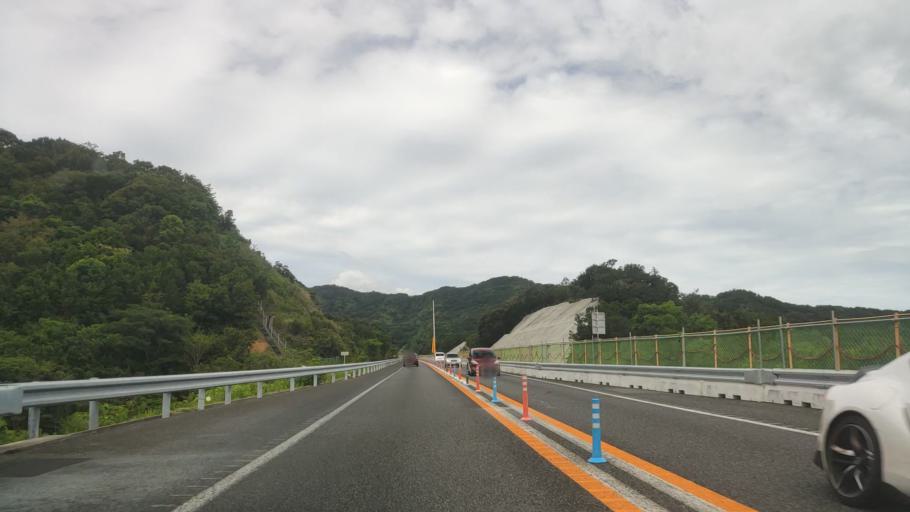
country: JP
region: Wakayama
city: Gobo
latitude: 33.8410
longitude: 135.2200
